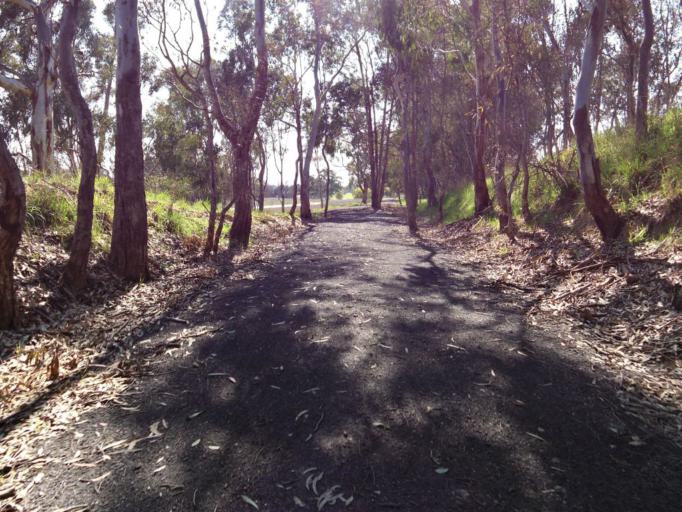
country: AU
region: Victoria
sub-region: Murrindindi
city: Alexandra
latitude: -37.1314
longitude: 145.5940
